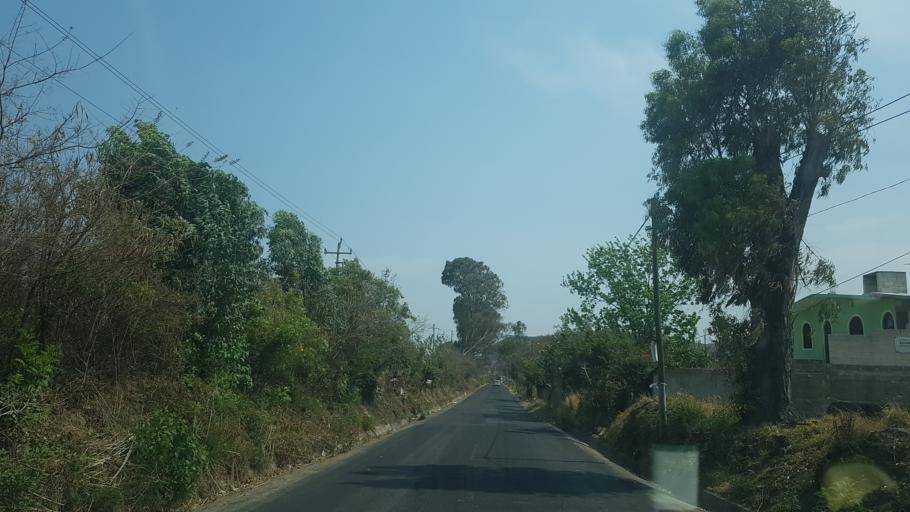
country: MX
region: Puebla
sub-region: Tianguismanalco
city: San Martin Tlapala
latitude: 18.9562
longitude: -98.4585
